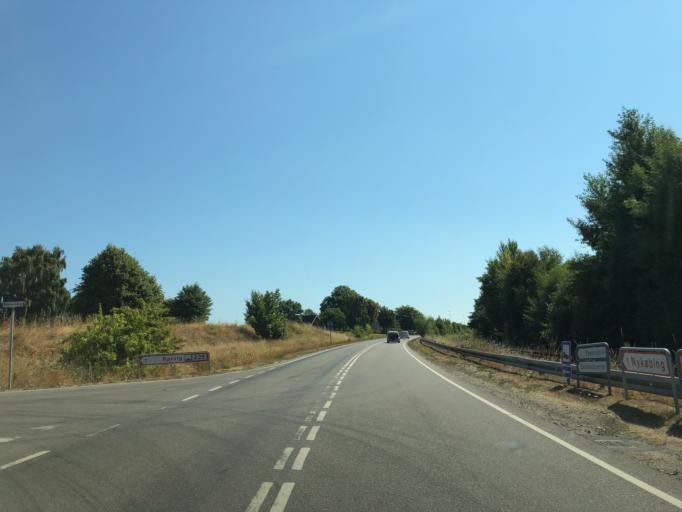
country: DK
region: Zealand
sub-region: Odsherred Kommune
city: Nykobing Sjaelland
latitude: 55.9227
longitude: 11.6498
